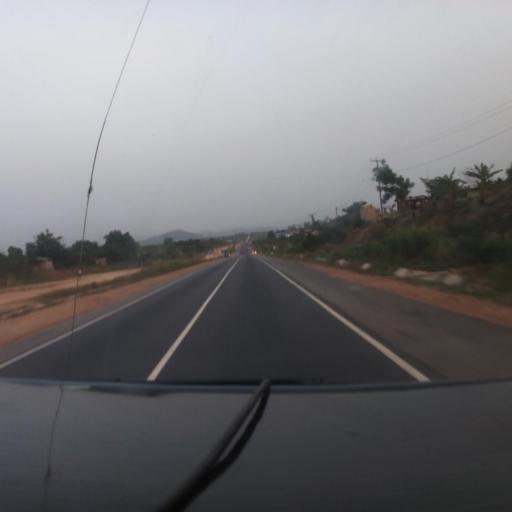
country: GH
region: Eastern
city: Nsawam
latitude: 5.8745
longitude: -0.3703
